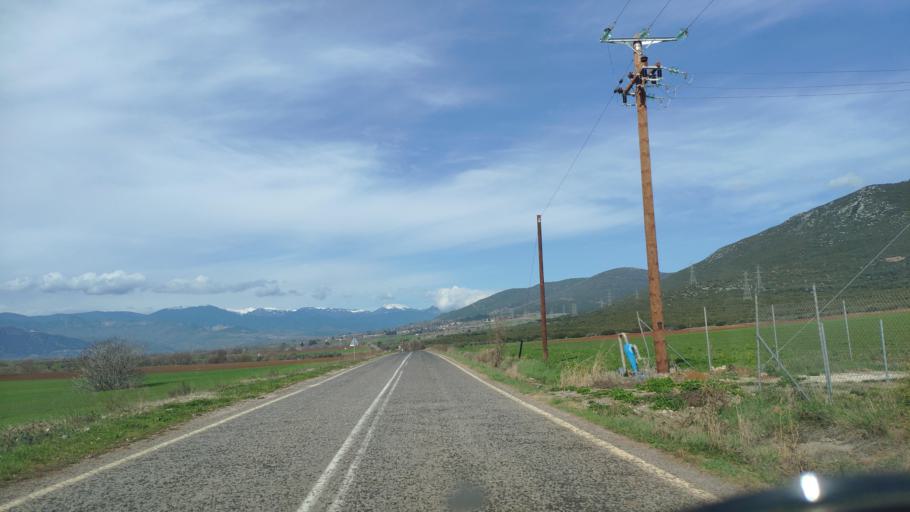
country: GR
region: Central Greece
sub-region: Nomos Fthiotidos
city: Amfikleia
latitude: 38.6962
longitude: 22.5225
